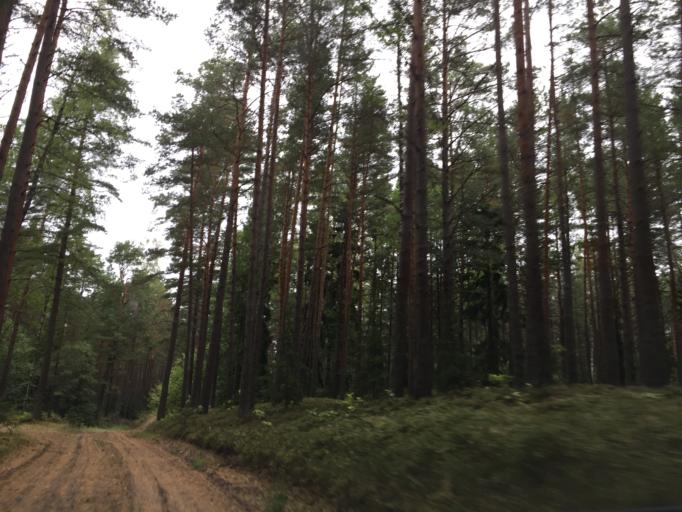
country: LV
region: Salacgrivas
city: Salacgriva
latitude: 57.7094
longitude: 24.3522
